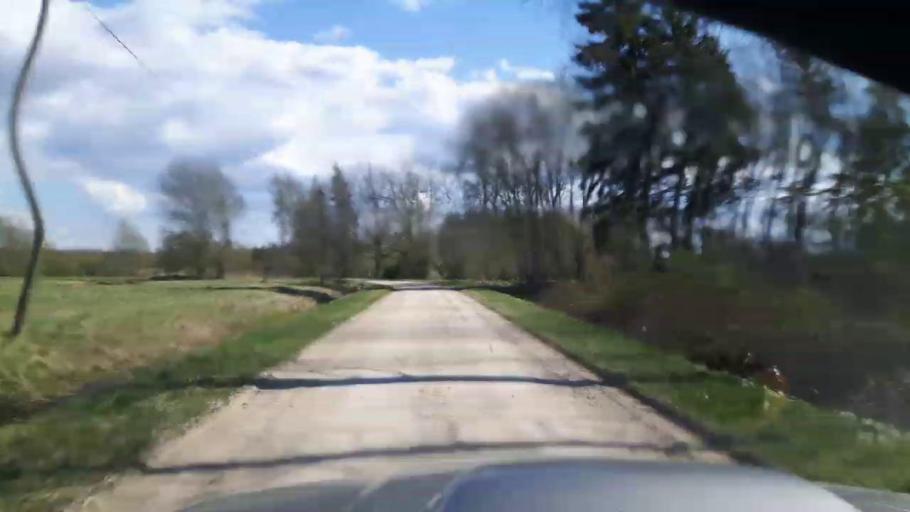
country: EE
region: Paernumaa
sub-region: Tootsi vald
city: Tootsi
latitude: 58.4603
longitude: 24.8019
